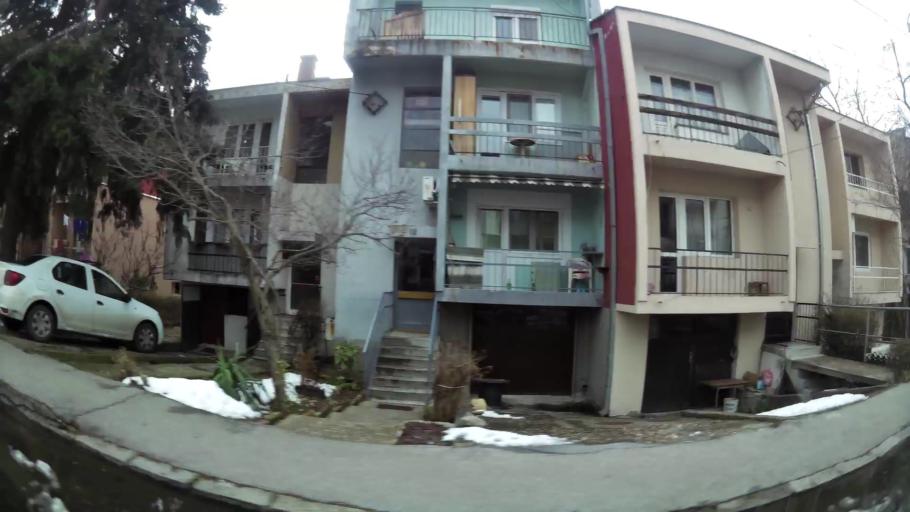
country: RS
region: Central Serbia
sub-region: Belgrade
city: Rakovica
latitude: 44.7495
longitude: 20.4180
